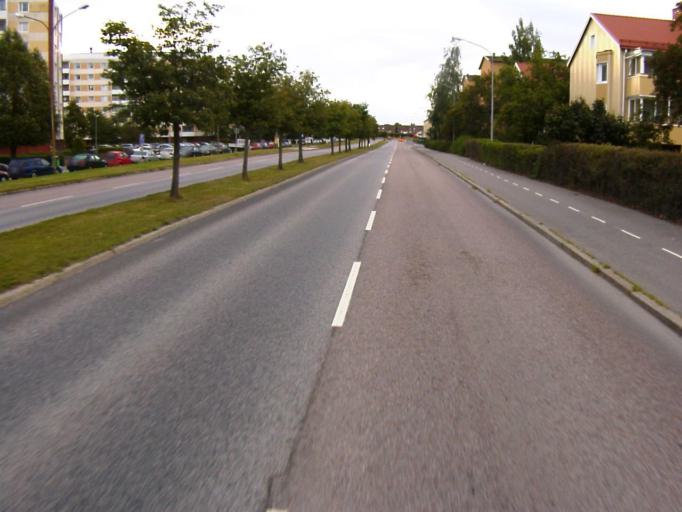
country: SE
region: Soedermanland
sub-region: Eskilstuna Kommun
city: Eskilstuna
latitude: 59.3820
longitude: 16.5141
